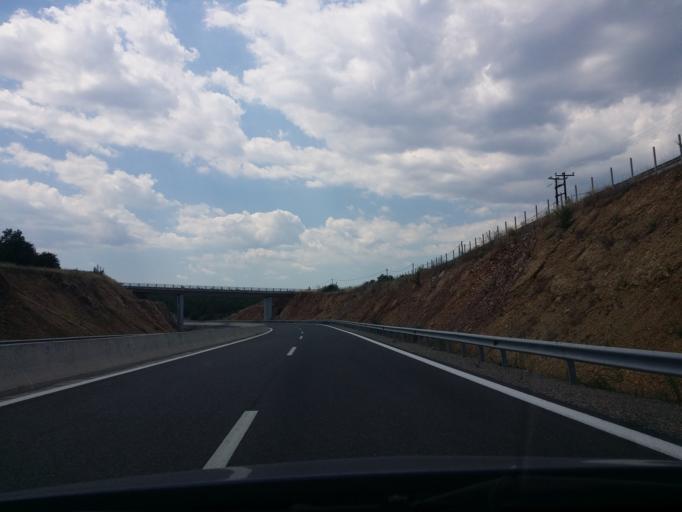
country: GR
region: Peloponnese
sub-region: Nomos Arkadias
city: Megalopoli
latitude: 37.3046
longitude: 22.1988
